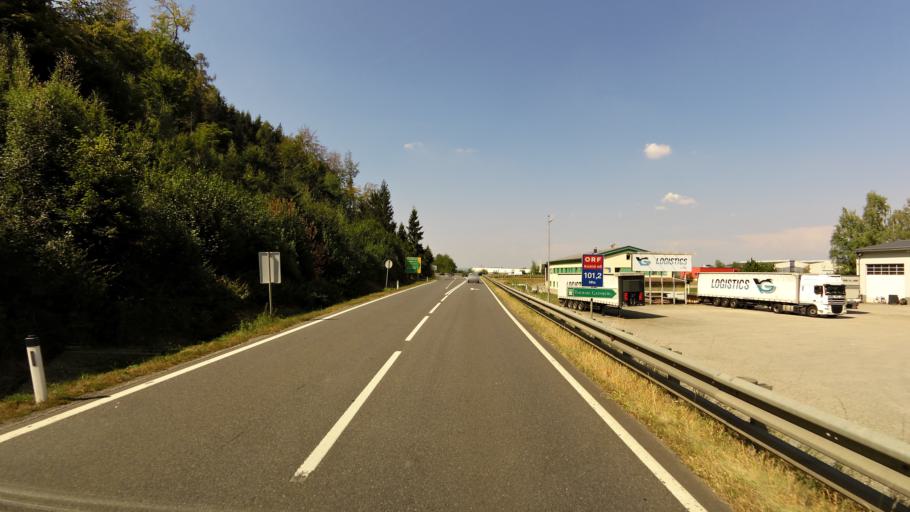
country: AT
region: Upper Austria
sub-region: Politischer Bezirk Braunau am Inn
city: Braunau am Inn
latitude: 48.1666
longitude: 13.1161
